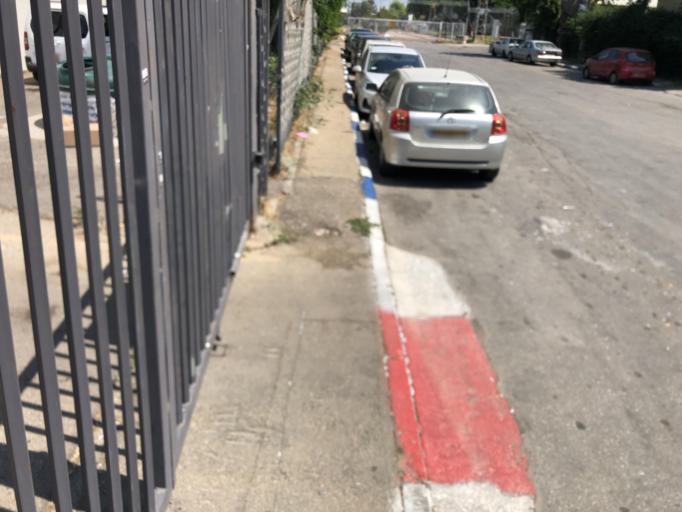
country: IL
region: Central District
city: Yehud
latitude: 32.0293
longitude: 34.9005
